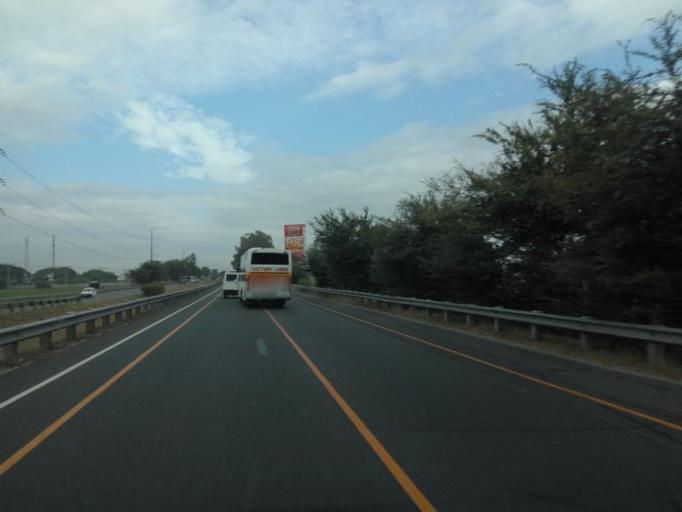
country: PH
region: Central Luzon
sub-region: Province of Pampanga
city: Pau
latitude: 15.0322
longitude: 120.7145
